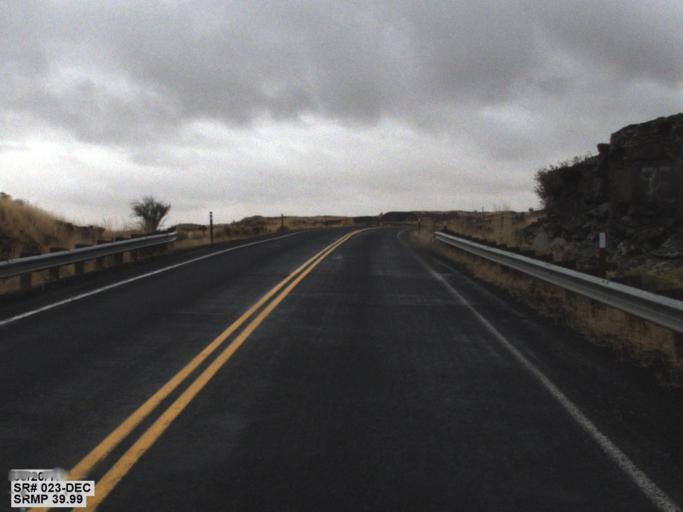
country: US
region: Washington
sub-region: Spokane County
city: Medical Lake
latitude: 47.2671
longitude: -117.9345
